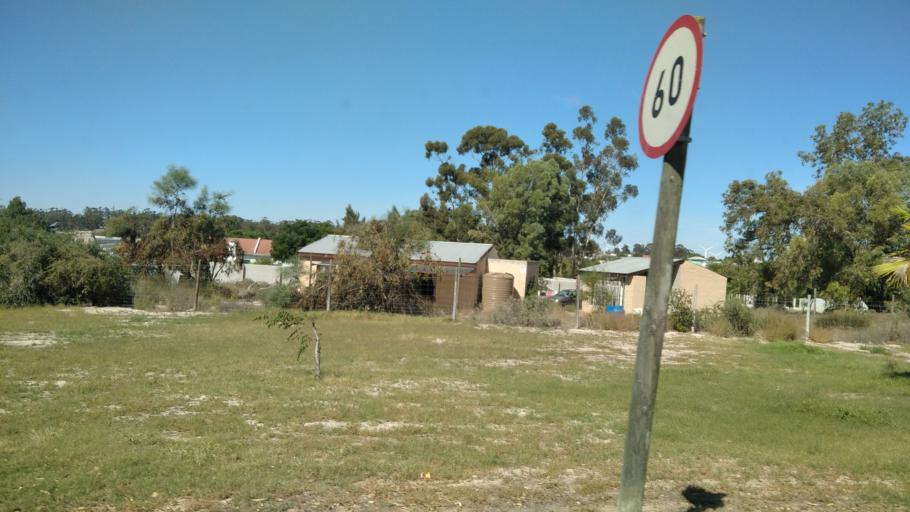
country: ZA
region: Western Cape
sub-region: West Coast District Municipality
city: Moorreesburg
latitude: -33.0567
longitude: 18.3430
